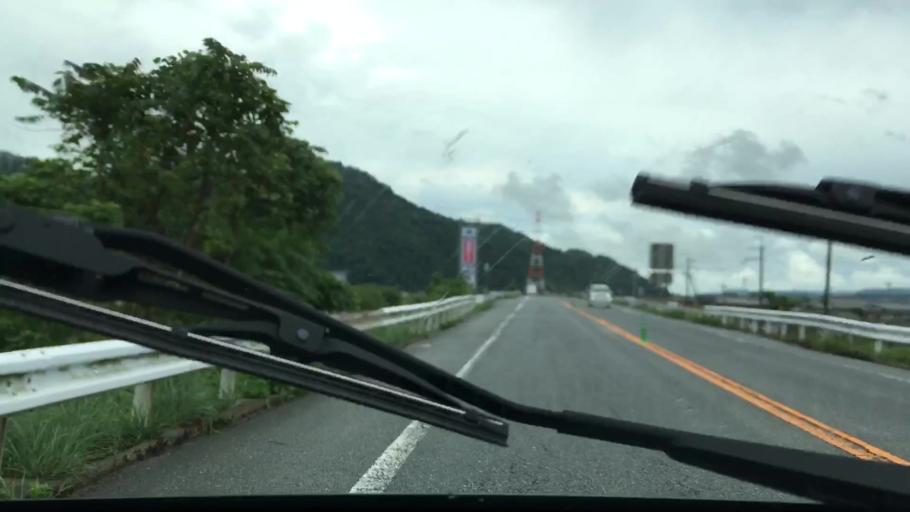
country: JP
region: Hyogo
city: Himeji
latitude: 34.9794
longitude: 134.7689
